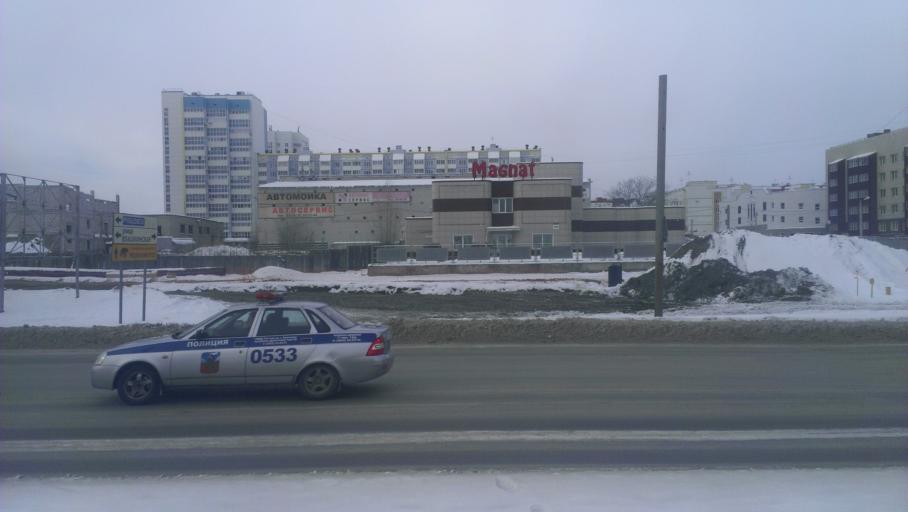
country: RU
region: Altai Krai
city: Novosilikatnyy
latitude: 53.3286
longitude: 83.6925
